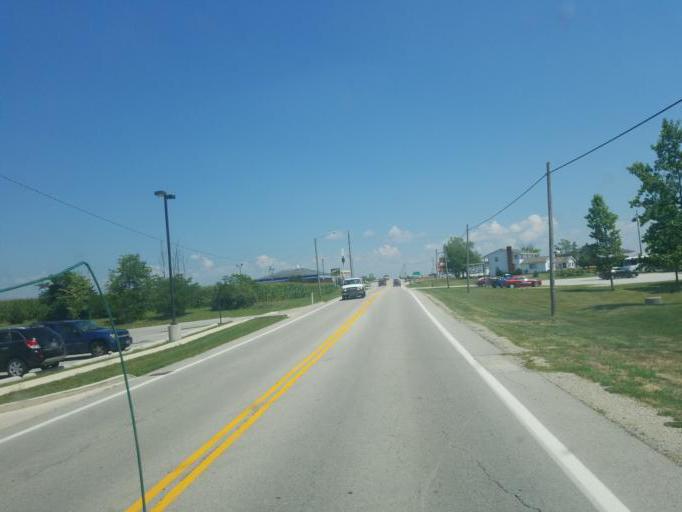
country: US
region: Ohio
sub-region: Shelby County
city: Anna
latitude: 40.3952
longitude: -84.1659
